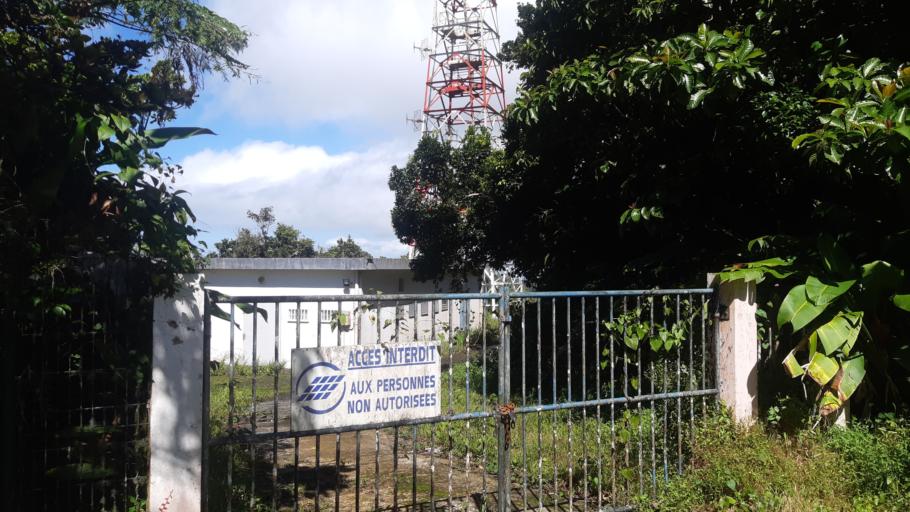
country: GP
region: Guadeloupe
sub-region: Guadeloupe
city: Pointe-Noire
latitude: 16.1865
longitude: -61.7497
